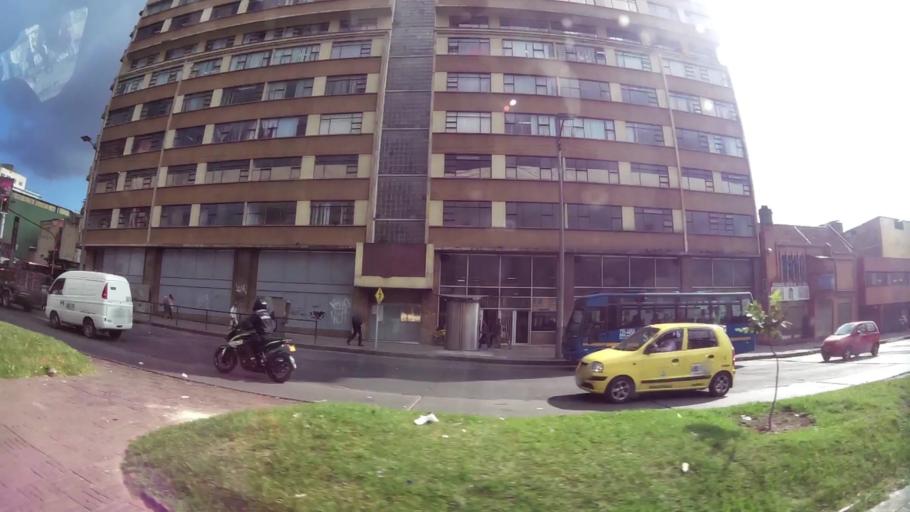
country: CO
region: Bogota D.C.
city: Bogota
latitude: 4.6090
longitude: -74.0768
